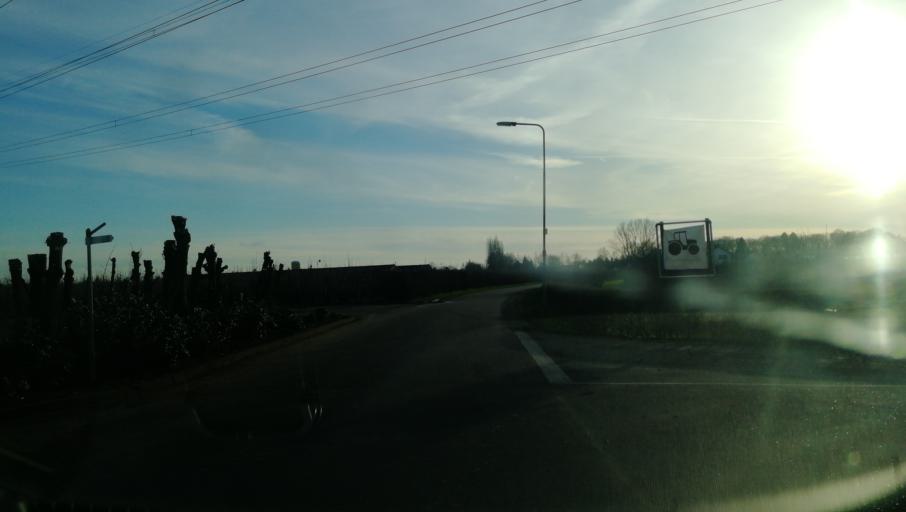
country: NL
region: Limburg
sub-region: Gemeente Venlo
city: Tegelen
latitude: 51.3366
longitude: 6.1068
